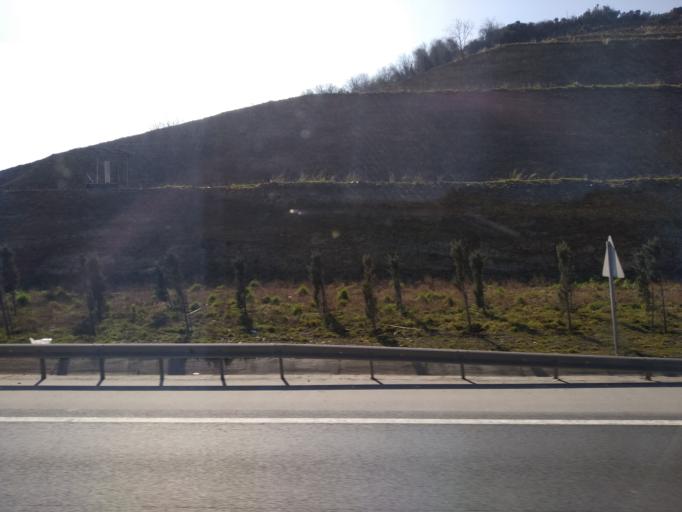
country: TR
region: Istanbul
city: Arikoey
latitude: 41.2286
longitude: 28.9755
